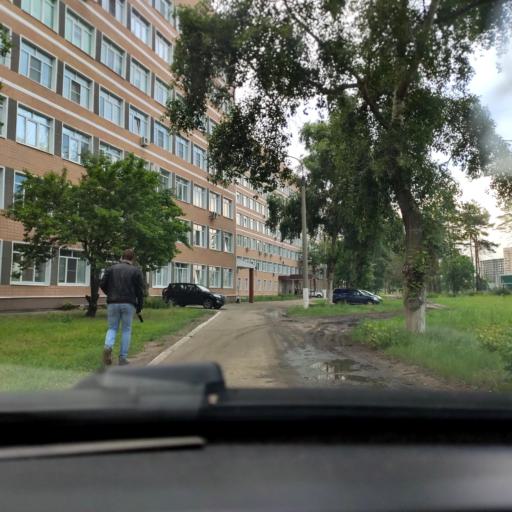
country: RU
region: Voronezj
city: Maslovka
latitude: 51.5852
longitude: 39.2416
